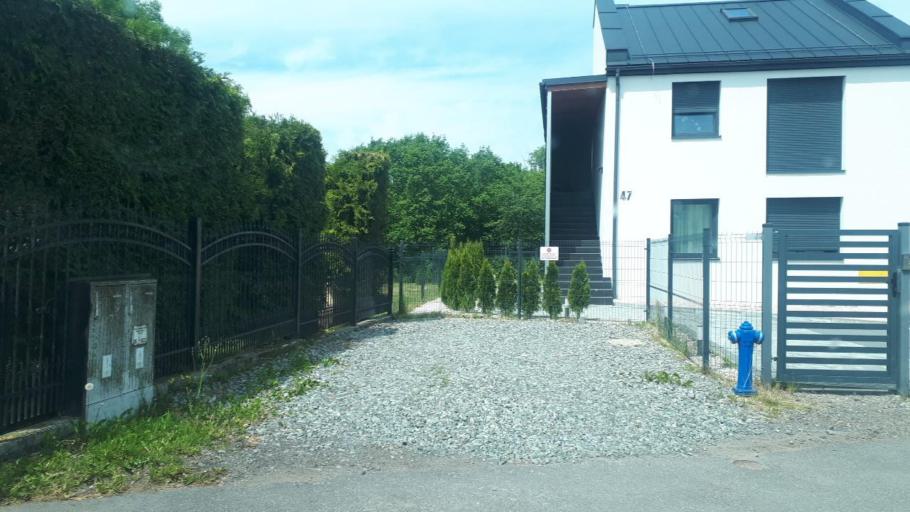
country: PL
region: Silesian Voivodeship
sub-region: Bielsko-Biala
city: Bielsko-Biala
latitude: 49.7977
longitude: 19.0321
